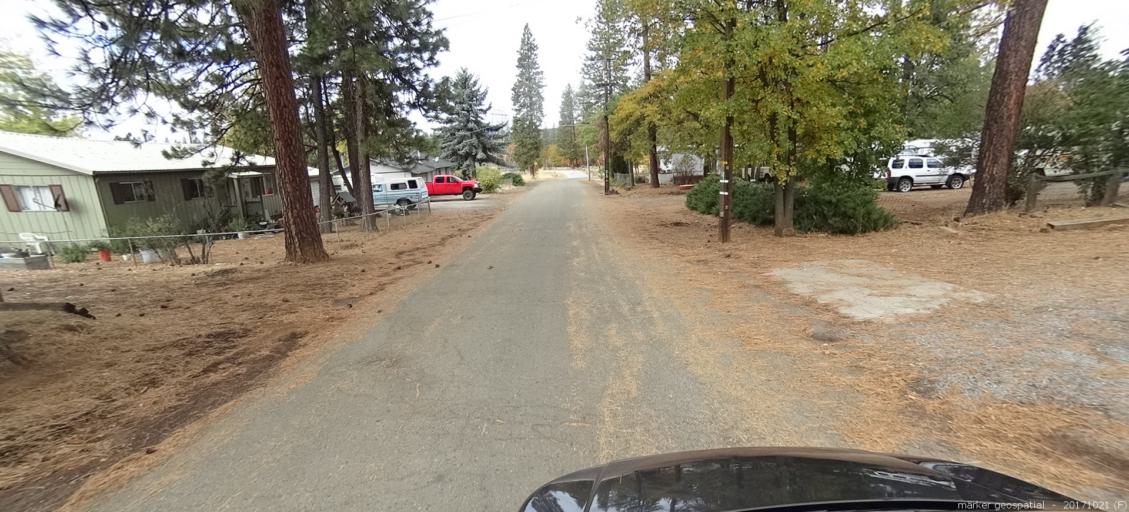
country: US
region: California
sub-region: Shasta County
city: Burney
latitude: 40.9210
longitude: -121.6263
